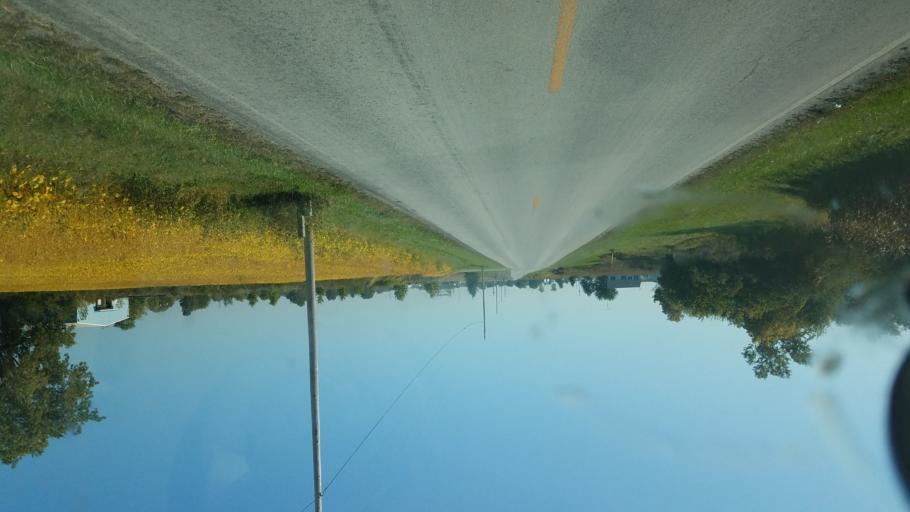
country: US
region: Ohio
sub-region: Hardin County
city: Kenton
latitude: 40.6307
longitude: -83.5771
